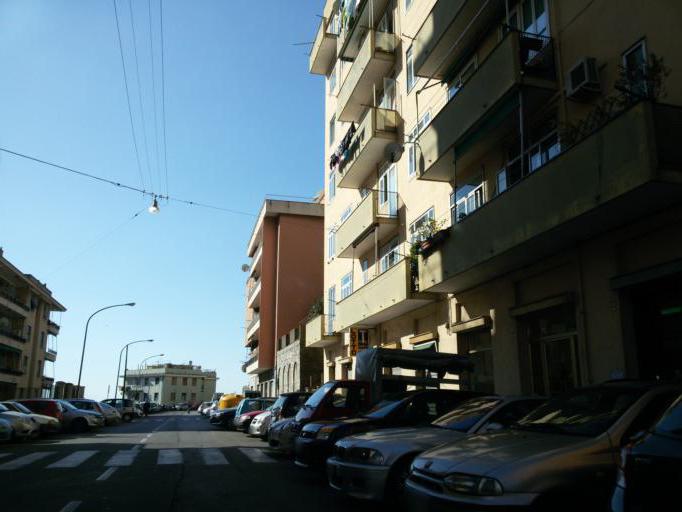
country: IT
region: Liguria
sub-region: Provincia di Genova
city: Genoa
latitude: 44.4218
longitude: 8.9167
